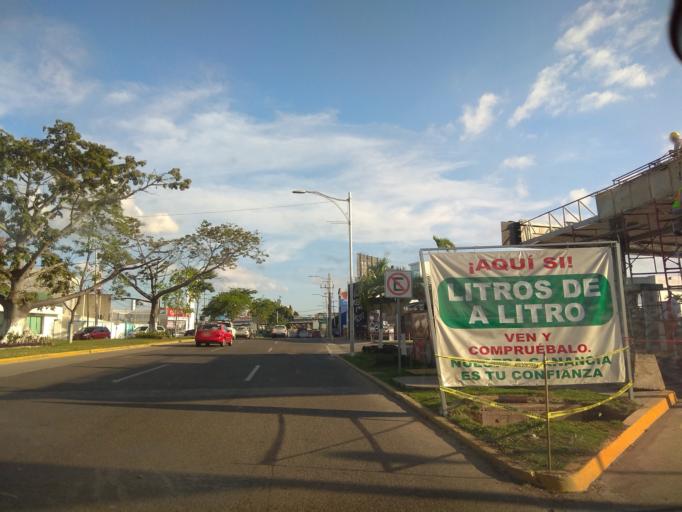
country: MX
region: Tabasco
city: Villahermosa
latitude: 17.9934
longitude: -92.9468
